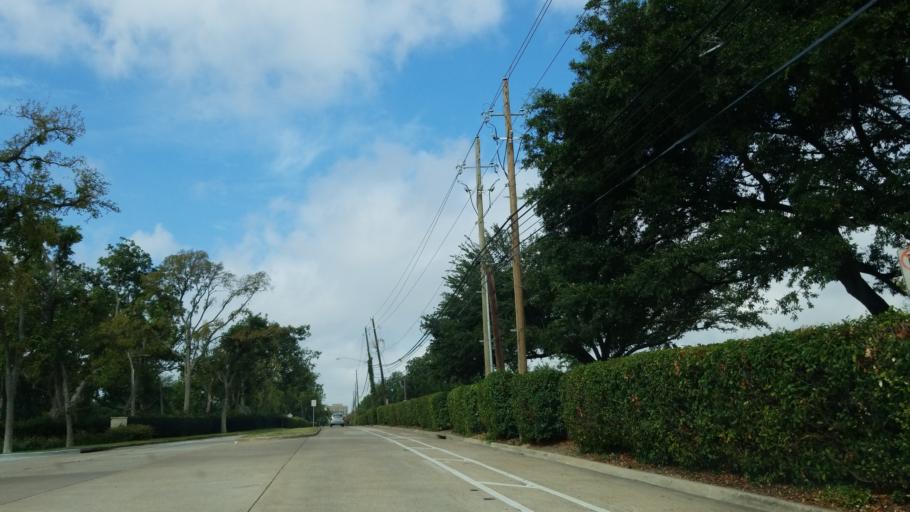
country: US
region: Texas
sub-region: Dallas County
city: Addison
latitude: 32.9332
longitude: -96.7930
